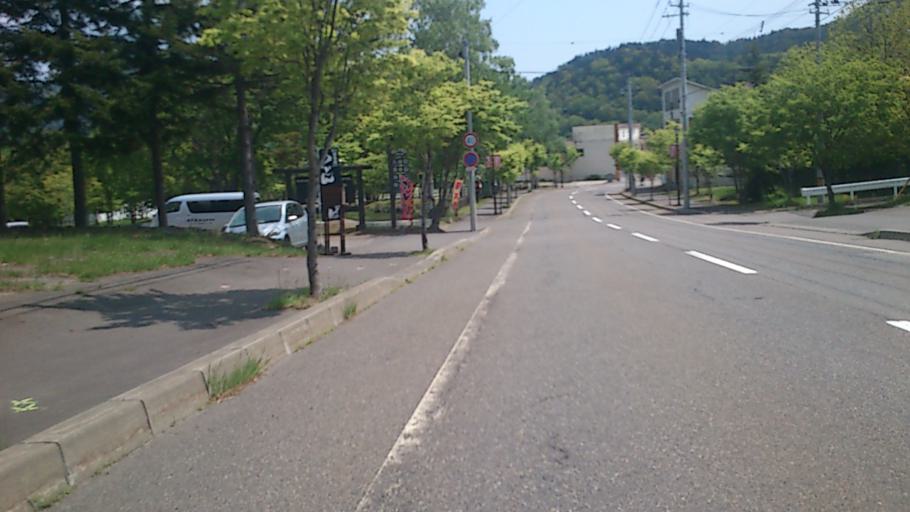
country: JP
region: Hokkaido
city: Otofuke
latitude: 43.3649
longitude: 143.1880
